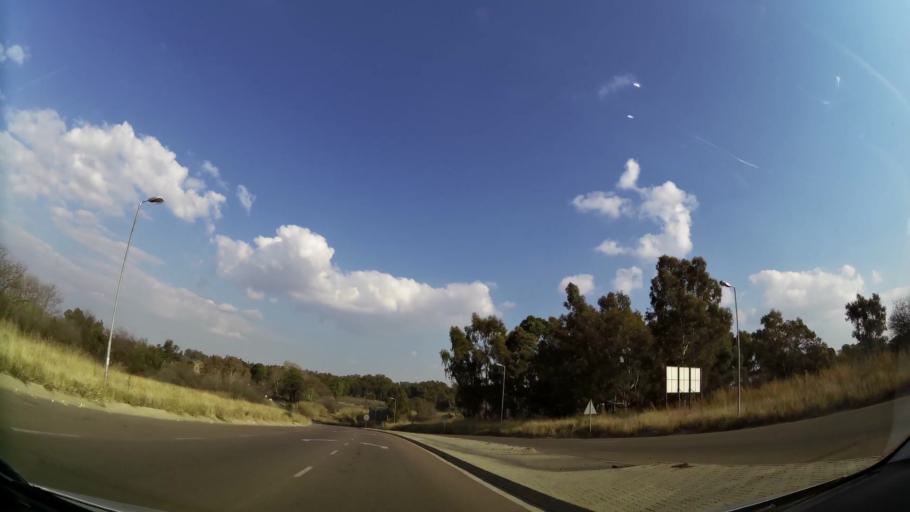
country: ZA
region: Gauteng
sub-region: City of Tshwane Metropolitan Municipality
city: Centurion
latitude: -25.9205
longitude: 28.2271
